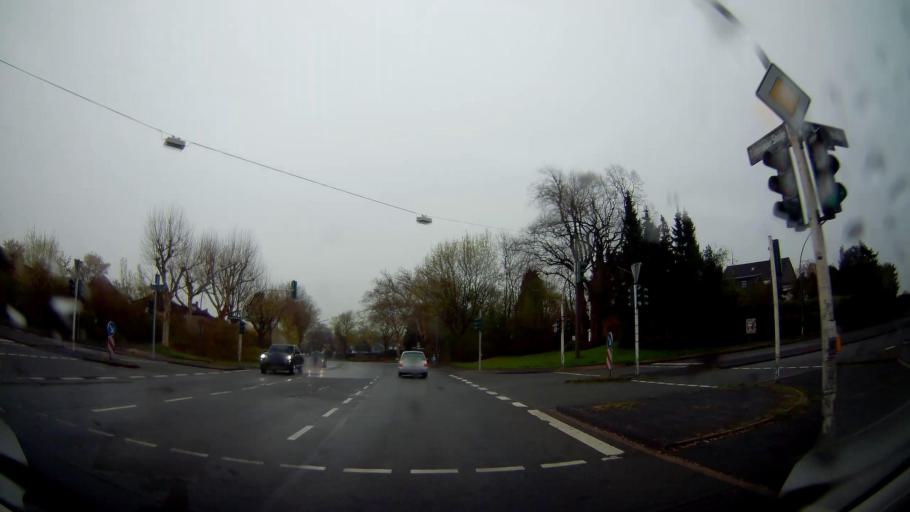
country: DE
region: North Rhine-Westphalia
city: Castrop-Rauxel
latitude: 51.5320
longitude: 7.3468
